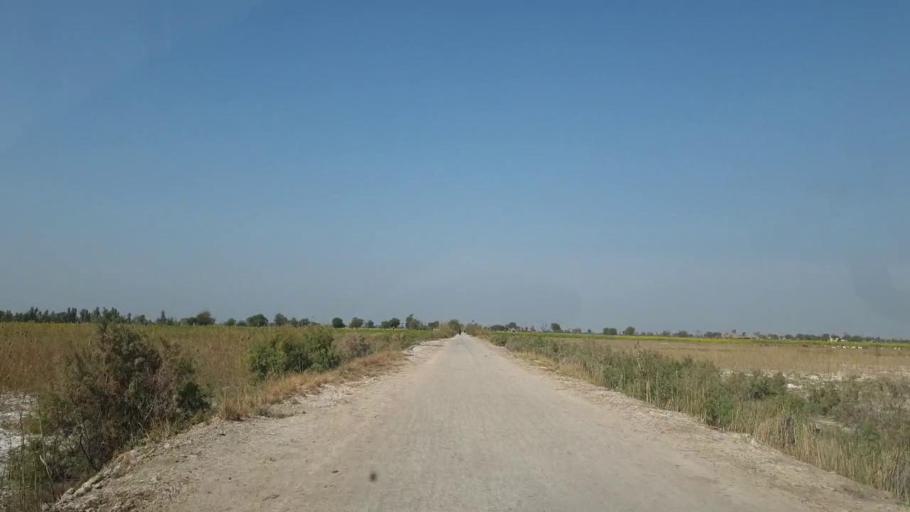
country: PK
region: Sindh
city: Mirpur Khas
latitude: 25.7161
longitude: 69.1393
